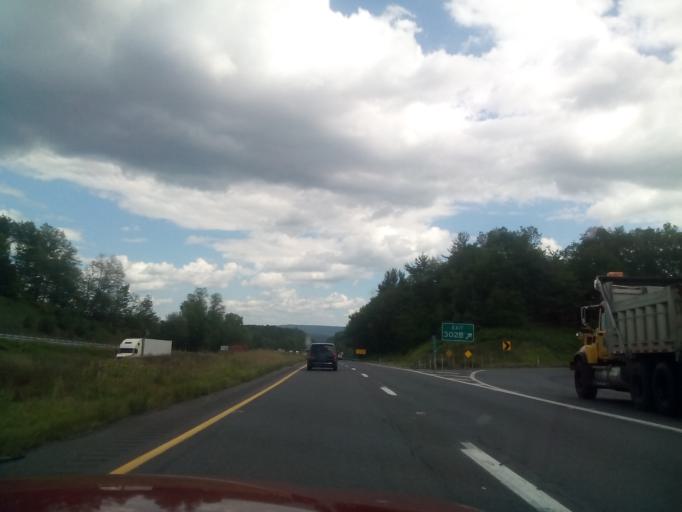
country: US
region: Pennsylvania
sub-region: Monroe County
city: Arlington Heights
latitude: 40.9972
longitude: -75.2684
